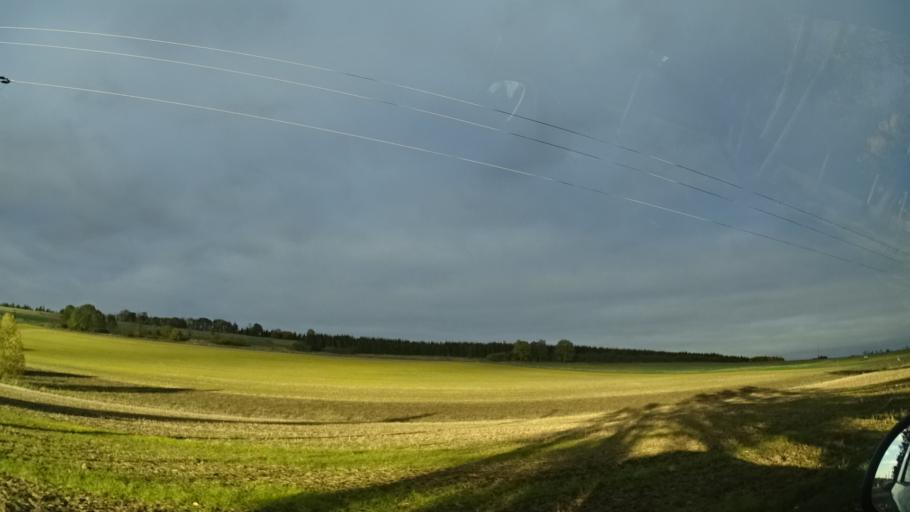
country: DE
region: Thuringia
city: Blankenhain
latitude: 50.8417
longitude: 11.3748
